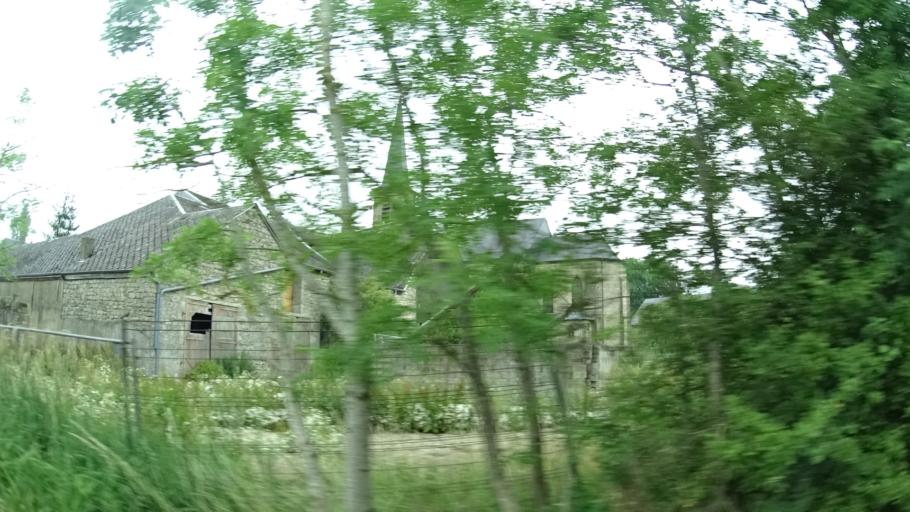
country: LU
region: Luxembourg
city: Eischen
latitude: 49.6496
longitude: 5.8700
